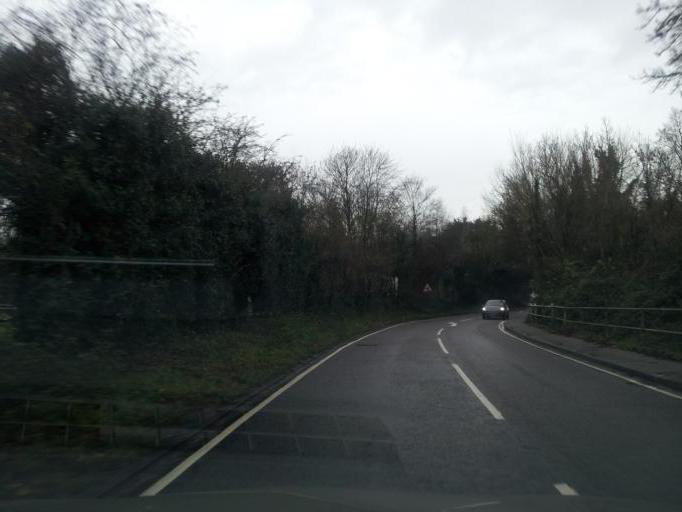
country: GB
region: England
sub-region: Essex
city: Earls Colne
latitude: 51.9379
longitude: 0.6543
